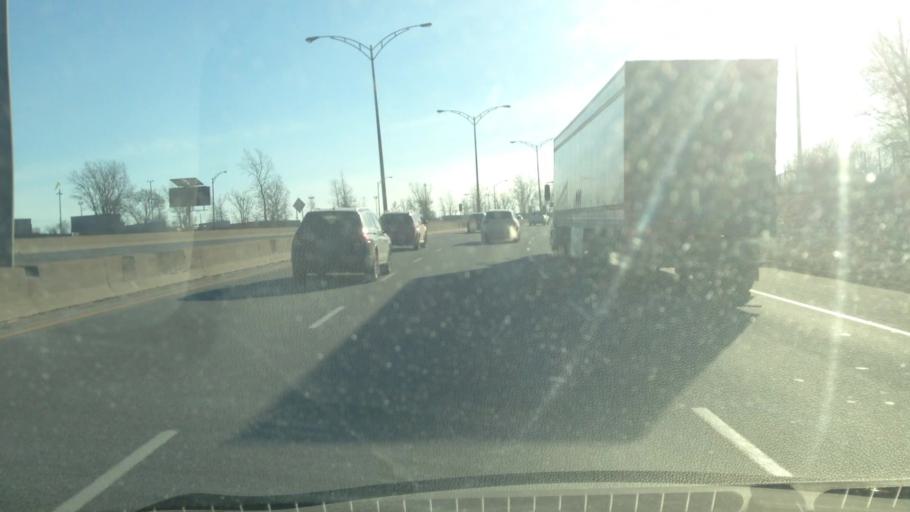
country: CA
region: Quebec
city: Cote-Saint-Luc
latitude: 45.4665
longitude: -73.6973
